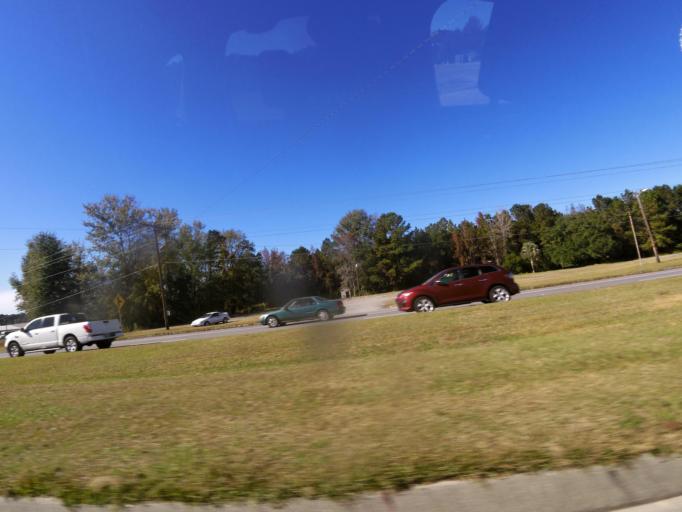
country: US
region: Georgia
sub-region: Bryan County
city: Richmond Hill
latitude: 31.9412
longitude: -81.3173
